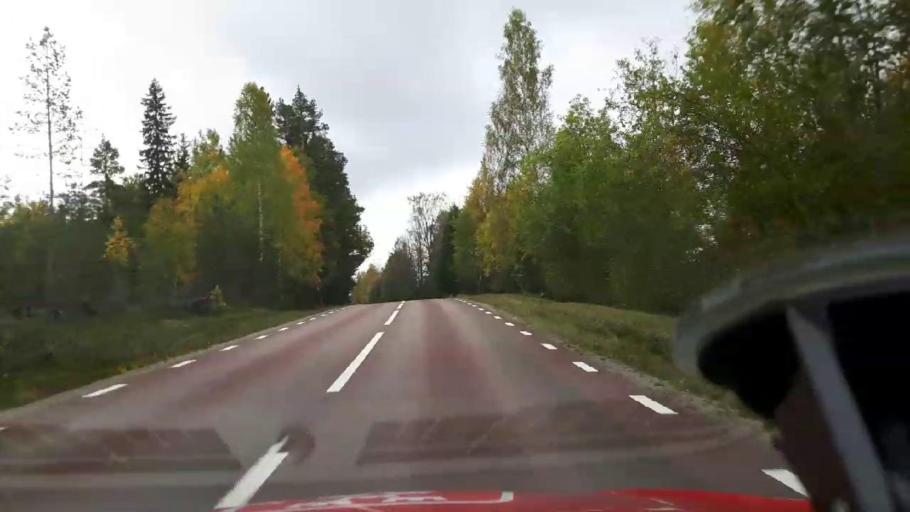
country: SE
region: Jaemtland
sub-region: Harjedalens Kommun
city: Sveg
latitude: 62.2002
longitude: 14.8532
